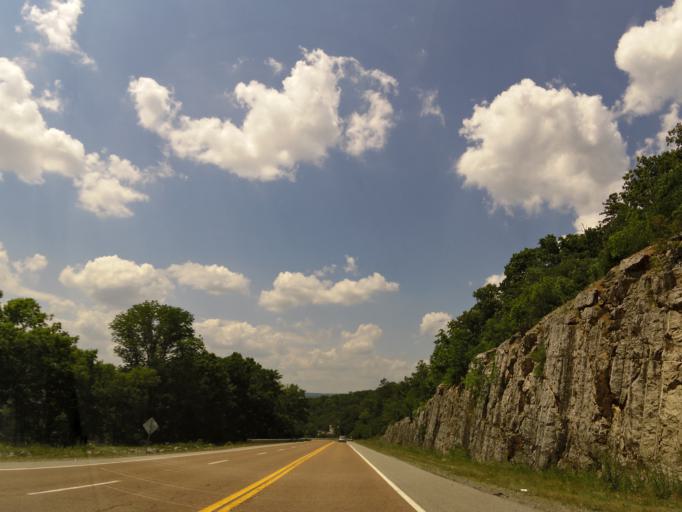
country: US
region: Tennessee
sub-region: Bledsoe County
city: Pikeville
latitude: 35.5777
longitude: -85.1584
